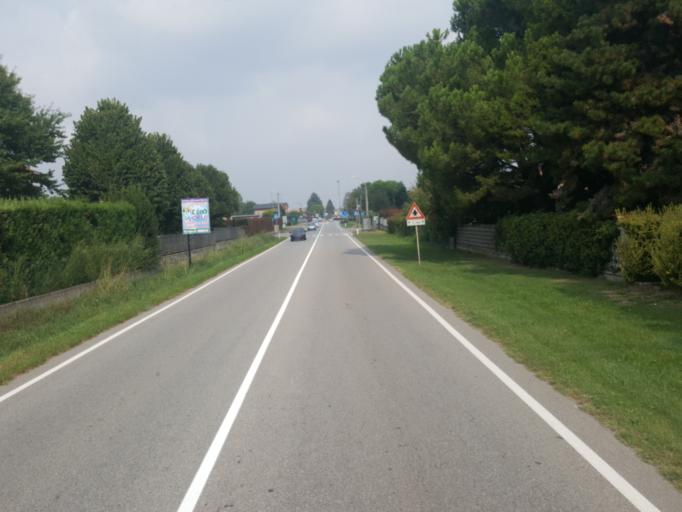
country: IT
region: Lombardy
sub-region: Provincia di Varese
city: Gorla Maggiore
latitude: 45.6601
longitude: 8.8978
